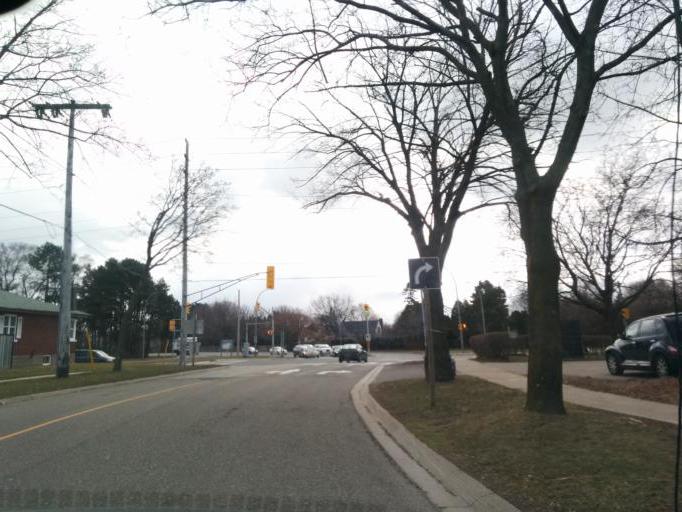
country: CA
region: Ontario
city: Etobicoke
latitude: 43.6000
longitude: -79.5697
